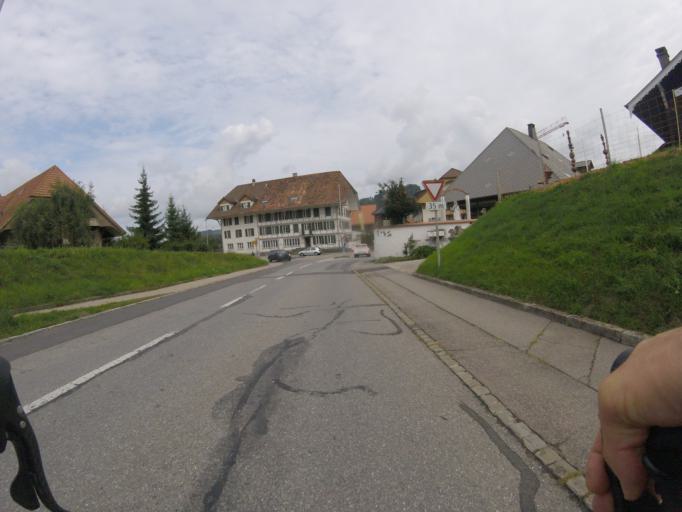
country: CH
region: Bern
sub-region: Emmental District
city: Lutzelfluh
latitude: 47.0031
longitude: 7.6790
